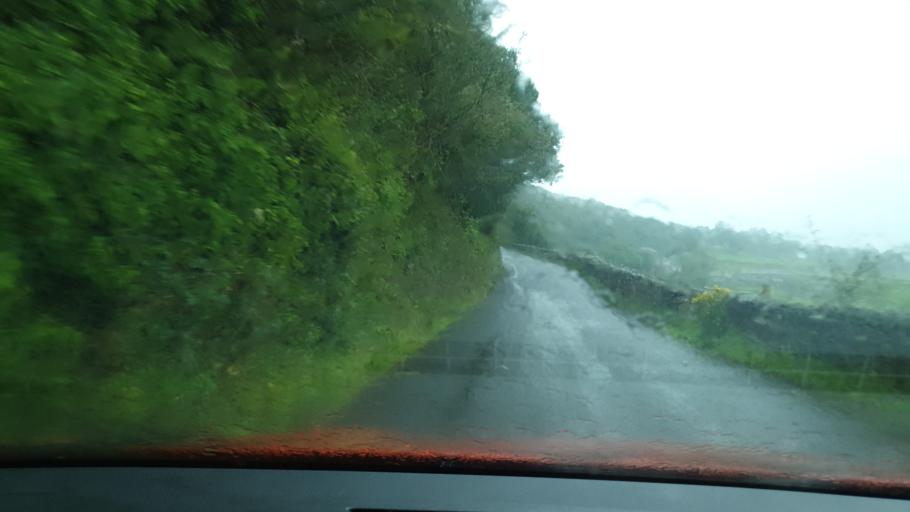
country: GB
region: England
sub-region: Cumbria
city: Millom
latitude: 54.2968
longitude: -3.2305
